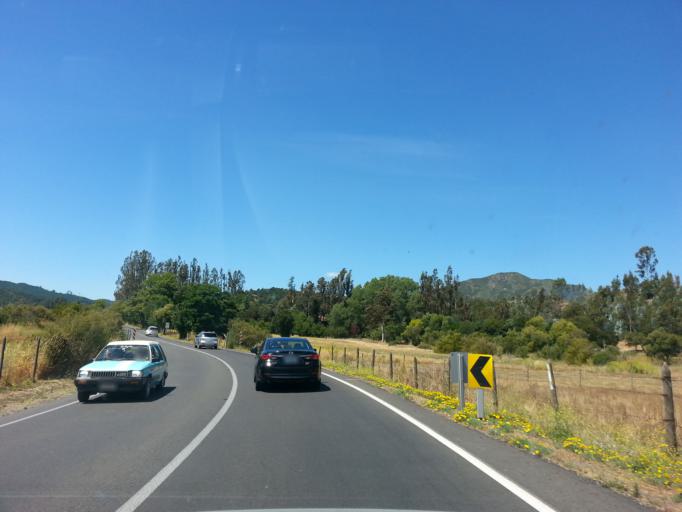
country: CL
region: Valparaiso
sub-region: Provincia de Marga Marga
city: Villa Alemana
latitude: -33.2250
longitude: -71.3940
